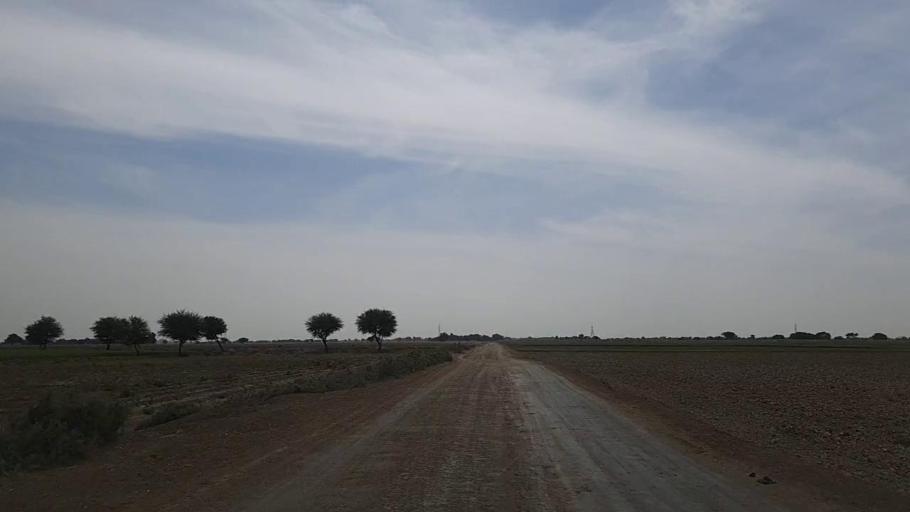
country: PK
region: Sindh
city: Samaro
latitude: 25.3015
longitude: 69.4529
